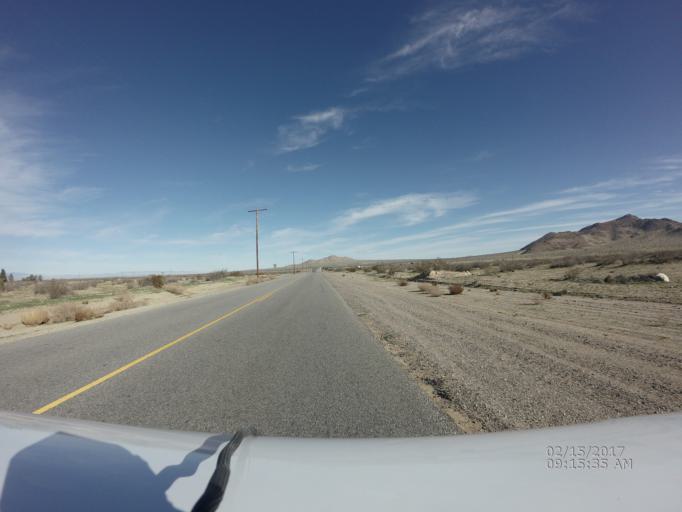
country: US
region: California
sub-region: Los Angeles County
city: Lake Los Angeles
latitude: 34.6571
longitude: -117.8275
